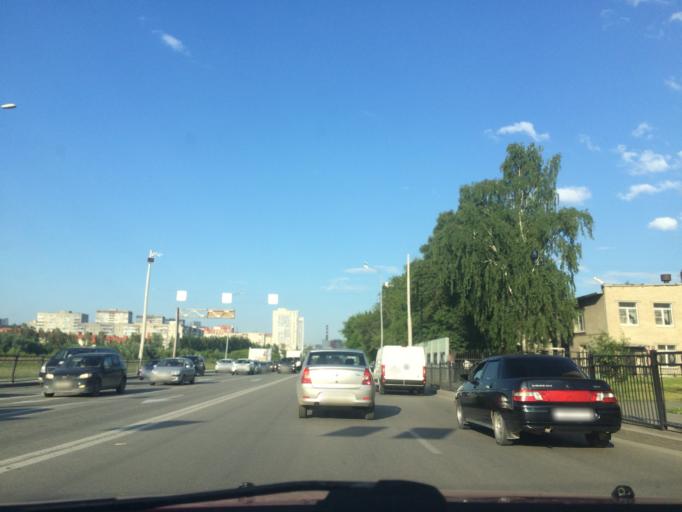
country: RU
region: Sverdlovsk
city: Yekaterinburg
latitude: 56.8168
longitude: 60.6213
